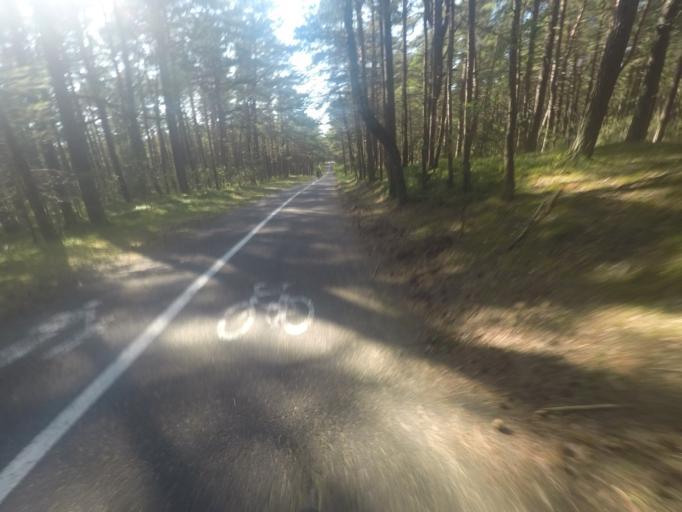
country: LT
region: Klaipedos apskritis
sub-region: Klaipeda
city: Klaipeda
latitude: 55.5473
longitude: 21.1075
